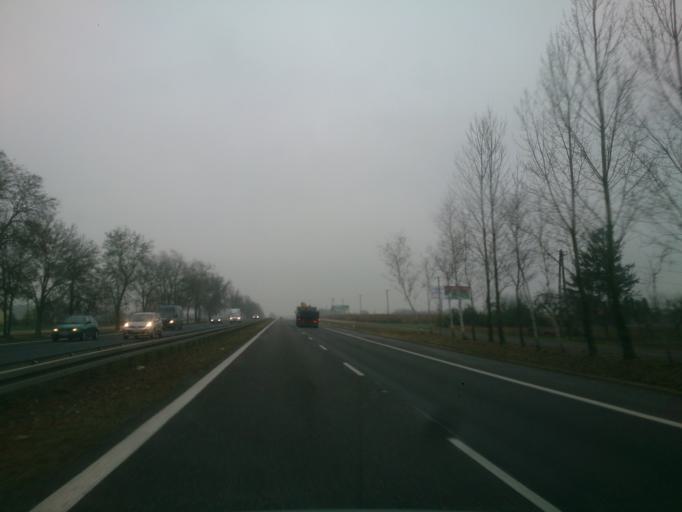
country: PL
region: Masovian Voivodeship
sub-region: Powiat plonski
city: Zaluski
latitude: 52.5570
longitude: 20.4951
